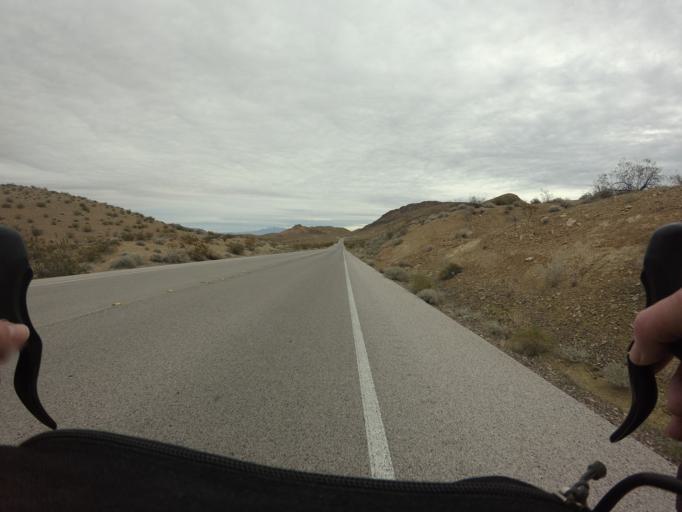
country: US
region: Nevada
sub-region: Clark County
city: Boulder City
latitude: 36.2284
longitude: -114.5802
